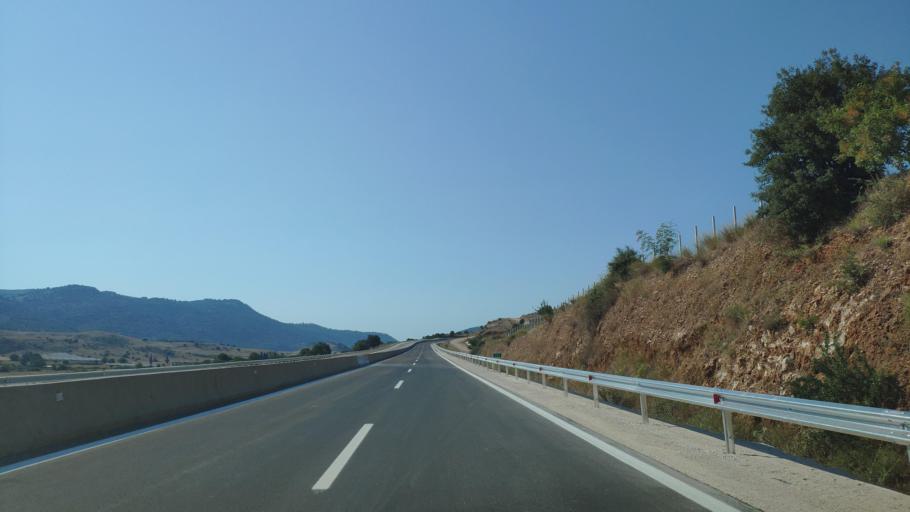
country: GR
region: West Greece
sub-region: Nomos Aitolias kai Akarnanias
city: Katouna
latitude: 38.7990
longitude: 21.1356
